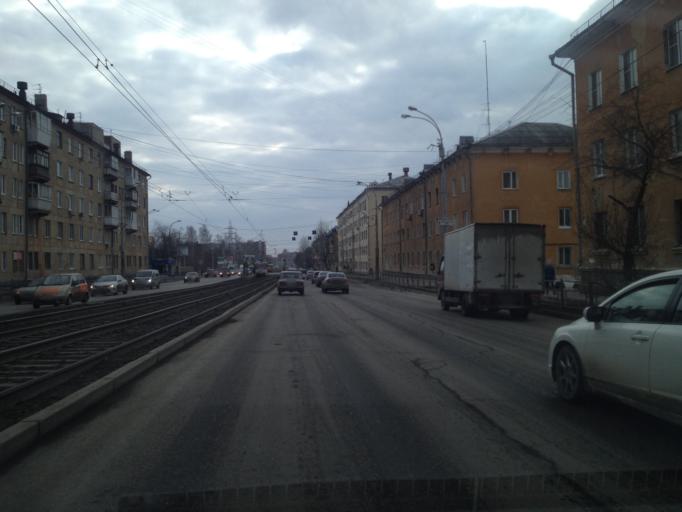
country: RU
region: Sverdlovsk
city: Yekaterinburg
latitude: 56.8852
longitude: 60.5635
